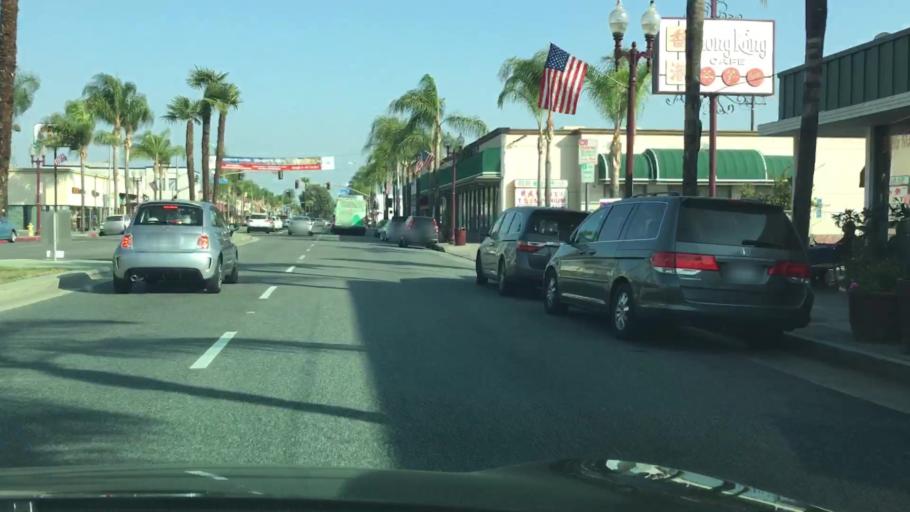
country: US
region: California
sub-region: Los Angeles County
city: Monterey Park
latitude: 34.0624
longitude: -118.1243
